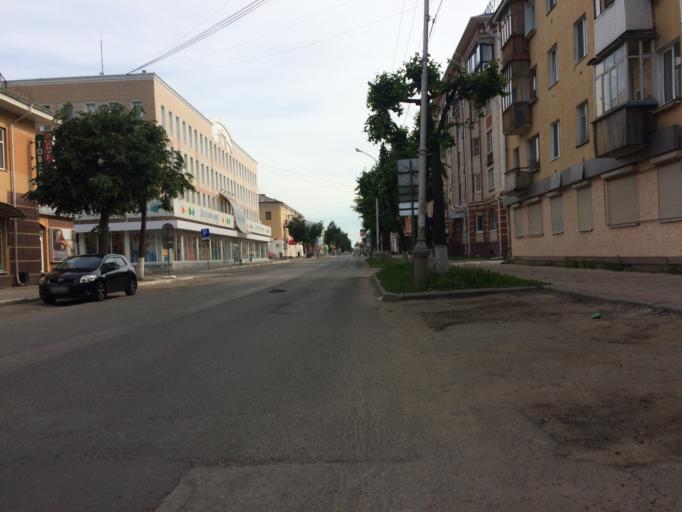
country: RU
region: Mariy-El
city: Yoshkar-Ola
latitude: 56.6332
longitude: 47.8962
